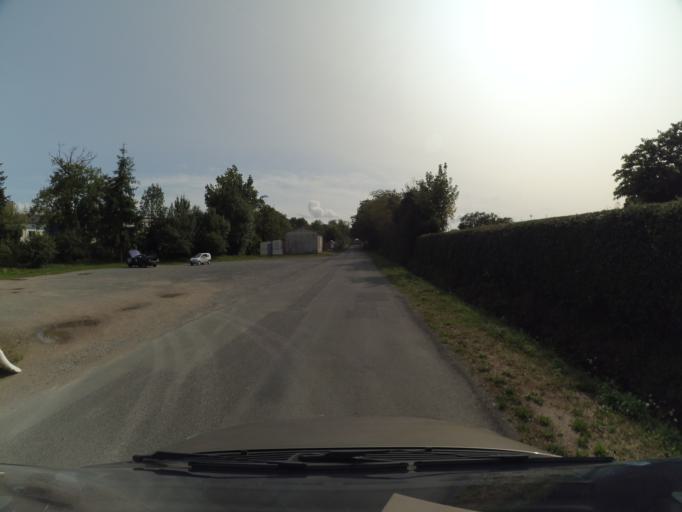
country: FR
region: Pays de la Loire
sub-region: Departement de la Vendee
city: La Bruffiere
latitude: 47.0110
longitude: -1.1968
